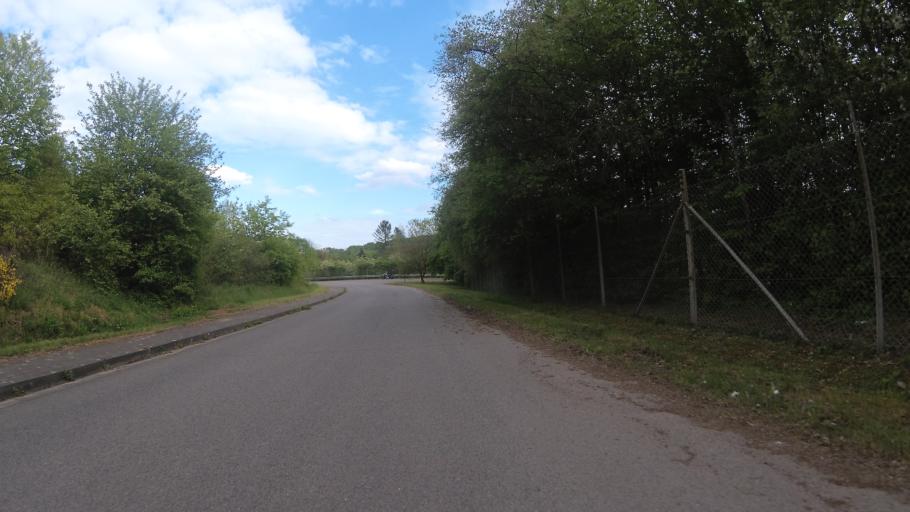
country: DE
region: Saarland
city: Neunkirchen
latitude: 49.3549
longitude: 7.2060
